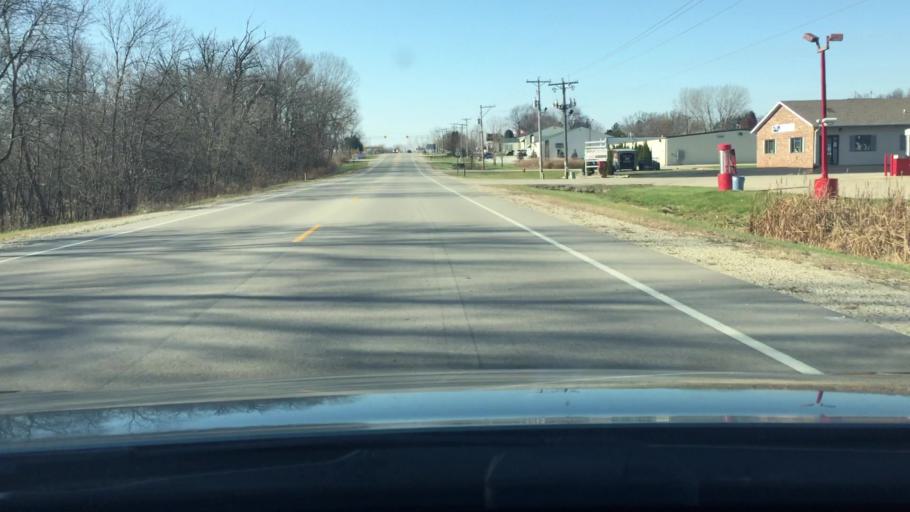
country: US
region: Wisconsin
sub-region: Jefferson County
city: Cambridge
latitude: 43.0088
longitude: -89.0163
